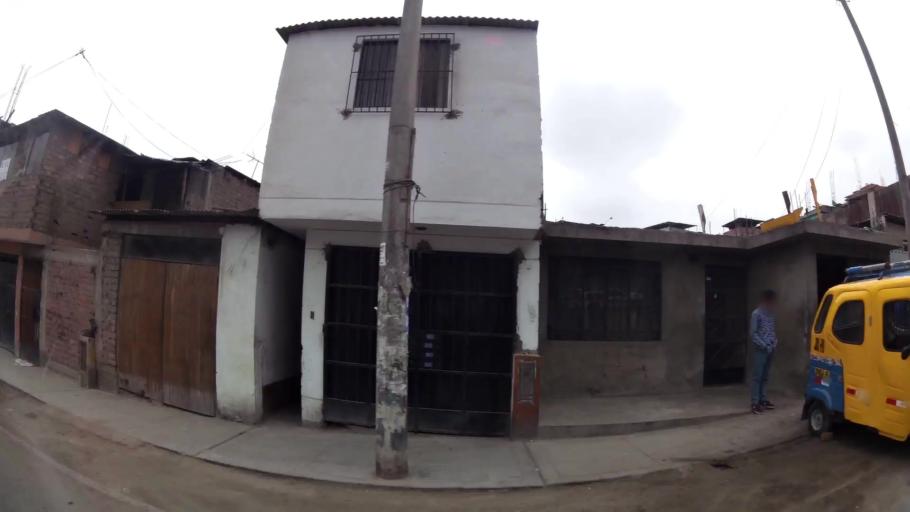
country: PE
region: Lima
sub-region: Lima
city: Surco
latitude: -12.1402
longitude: -76.9610
